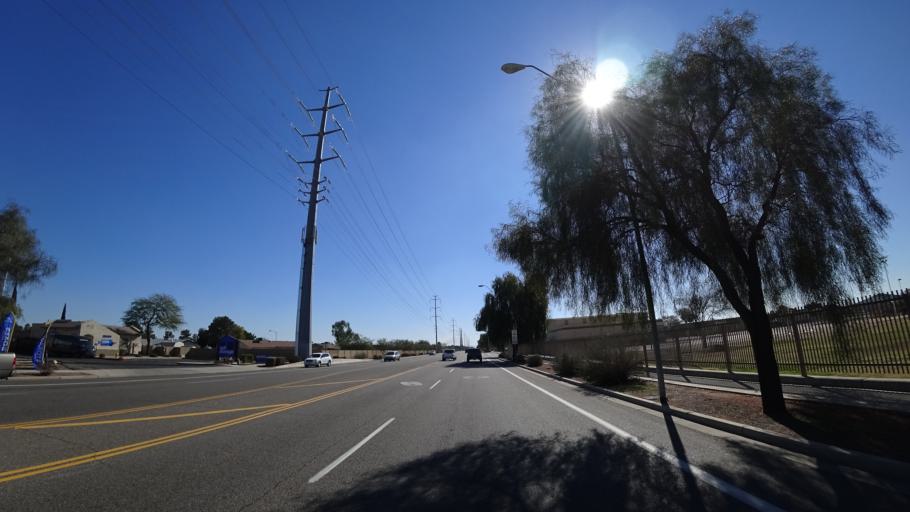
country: US
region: Arizona
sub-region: Maricopa County
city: Peoria
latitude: 33.6681
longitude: -112.1347
